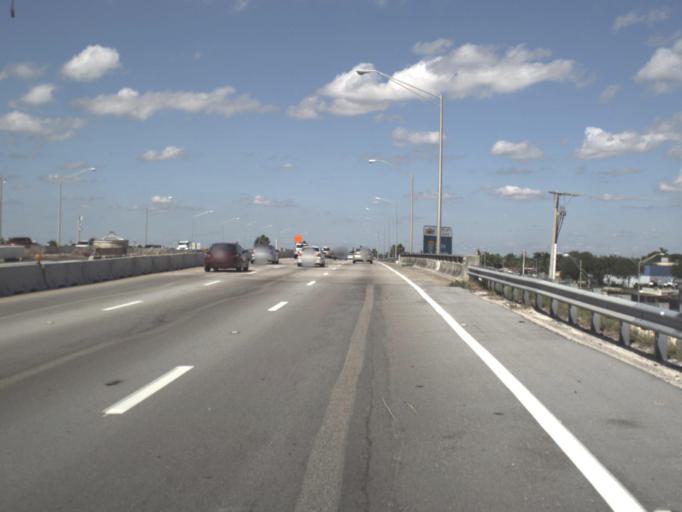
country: US
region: Florida
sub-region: Miami-Dade County
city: South Miami Heights
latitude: 25.5949
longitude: -80.3714
